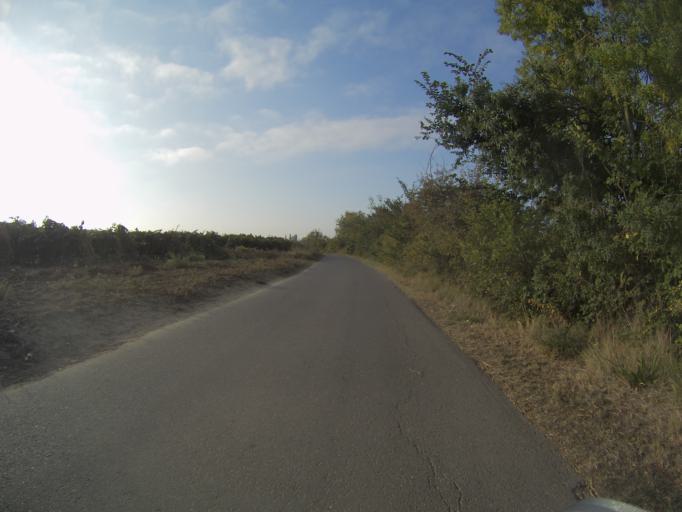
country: ES
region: Navarre
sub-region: Provincia de Navarra
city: Viana
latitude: 42.5013
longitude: -2.3882
